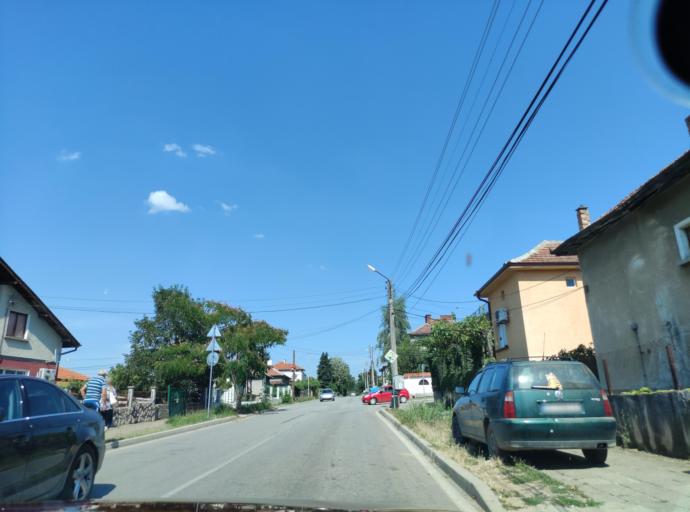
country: BG
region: Pleven
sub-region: Obshtina Cherven Bryag
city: Cherven Bryag
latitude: 43.2763
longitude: 24.0874
